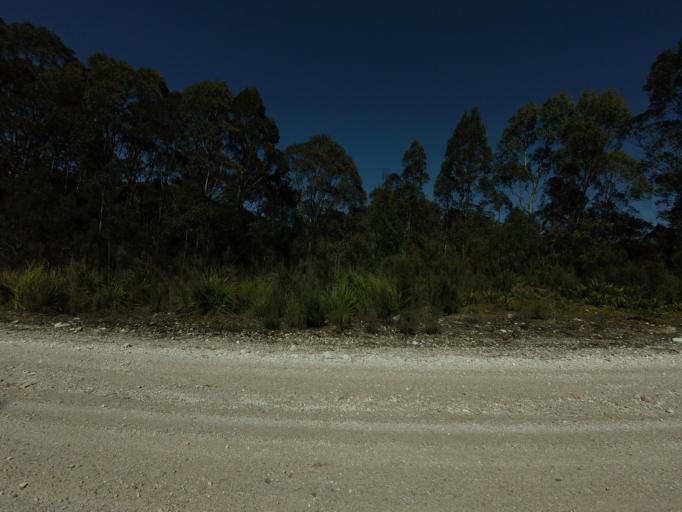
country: AU
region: Tasmania
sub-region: Huon Valley
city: Geeveston
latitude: -42.9130
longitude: 146.3626
